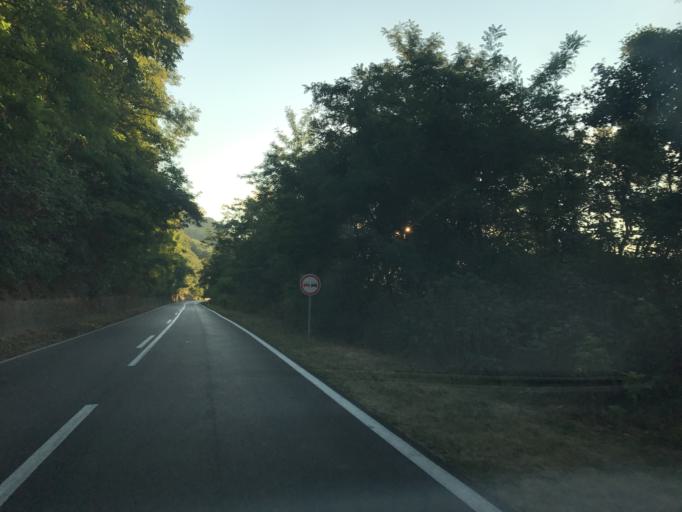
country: RO
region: Caras-Severin
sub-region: Comuna Berzasca
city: Liubcova
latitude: 44.6464
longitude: 21.8607
